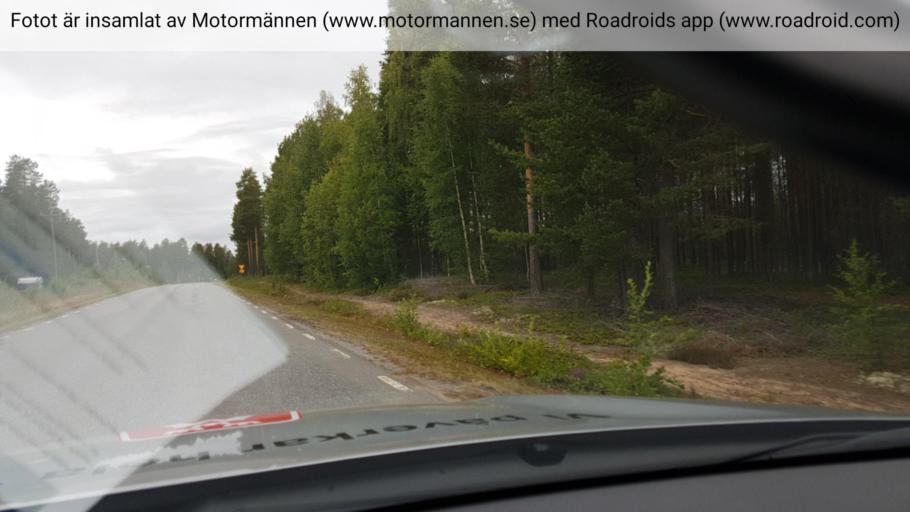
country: SE
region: Norrbotten
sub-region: Bodens Kommun
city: Boden
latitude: 65.8153
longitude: 21.5926
